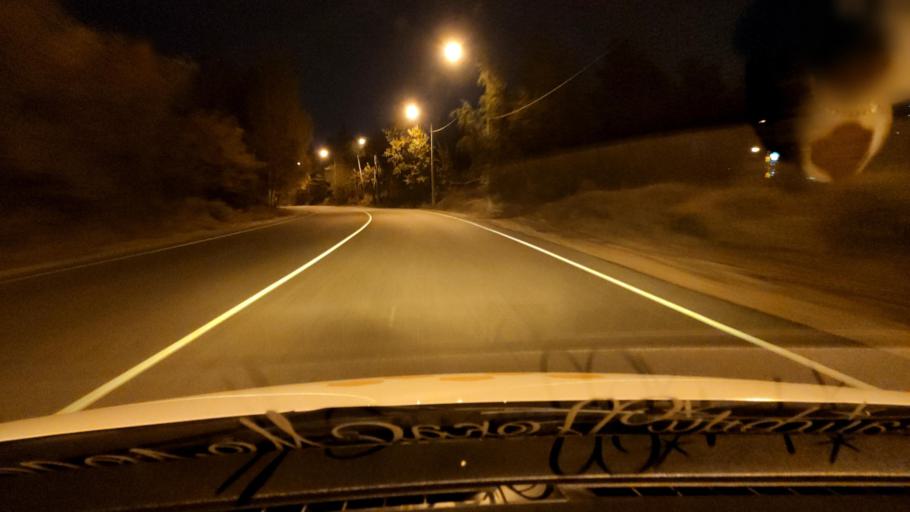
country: RU
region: Voronezj
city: Pridonskoy
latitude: 51.6798
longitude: 39.1136
